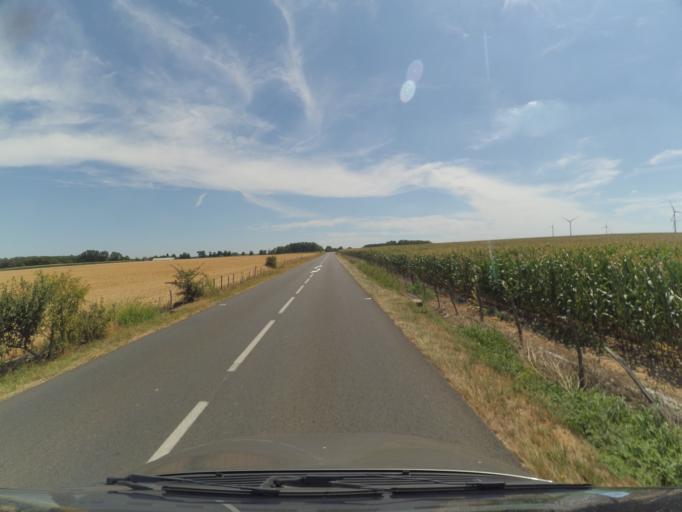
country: FR
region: Poitou-Charentes
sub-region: Departement de la Vienne
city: Saint-Maurice-la-Clouere
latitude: 46.3403
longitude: 0.4600
